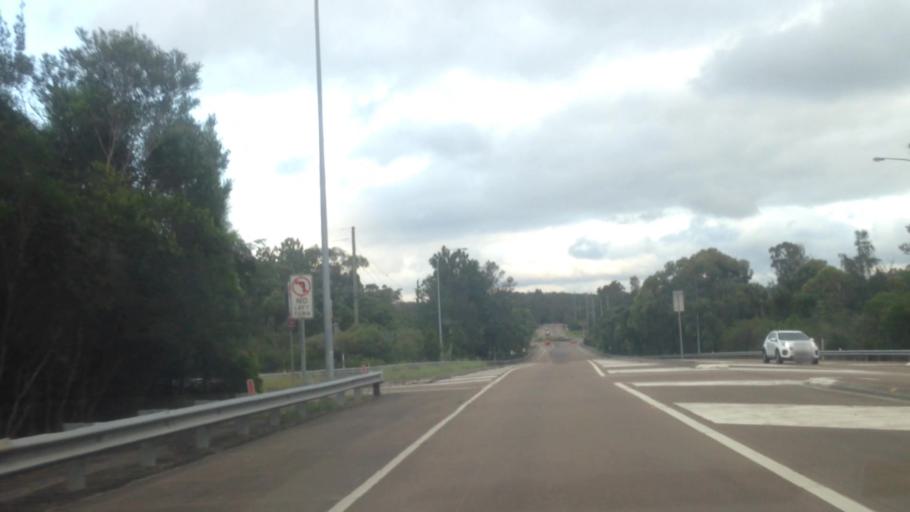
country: AU
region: New South Wales
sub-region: Lake Macquarie Shire
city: Cooranbong
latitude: -33.1182
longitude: 151.4661
